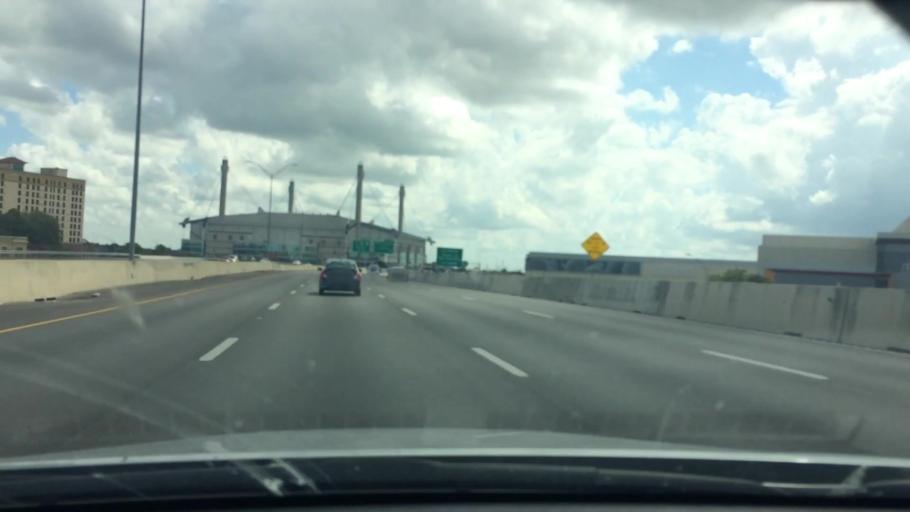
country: US
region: Texas
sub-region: Bexar County
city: San Antonio
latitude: 29.4237
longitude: -98.4813
